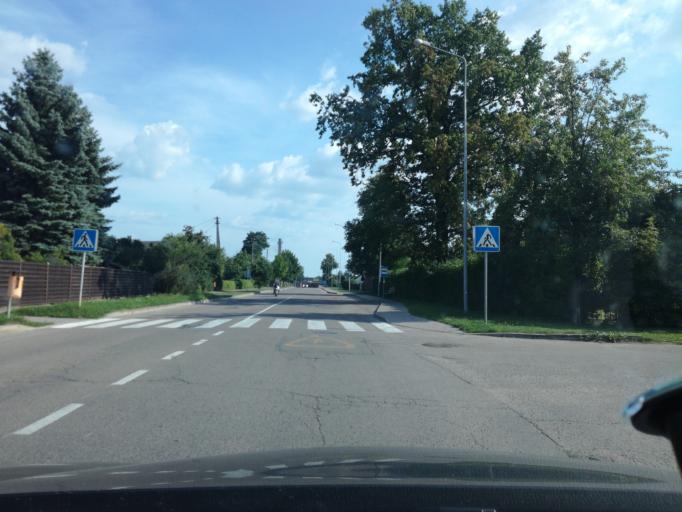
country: LT
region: Marijampoles apskritis
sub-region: Marijampole Municipality
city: Marijampole
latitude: 54.5422
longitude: 23.3492
